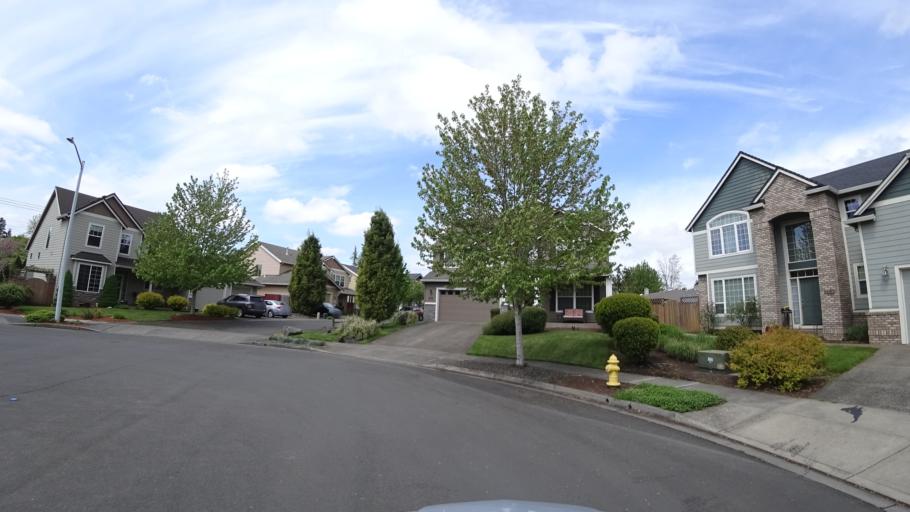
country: US
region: Oregon
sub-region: Washington County
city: Hillsboro
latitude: 45.5371
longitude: -122.9935
